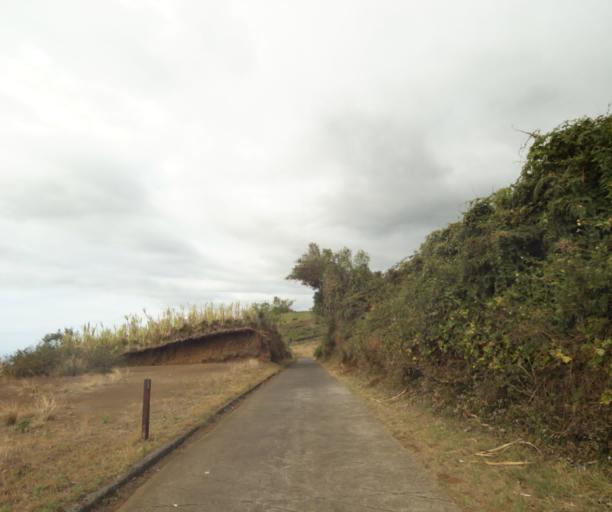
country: RE
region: Reunion
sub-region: Reunion
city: Saint-Paul
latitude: -21.0284
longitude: 55.3181
